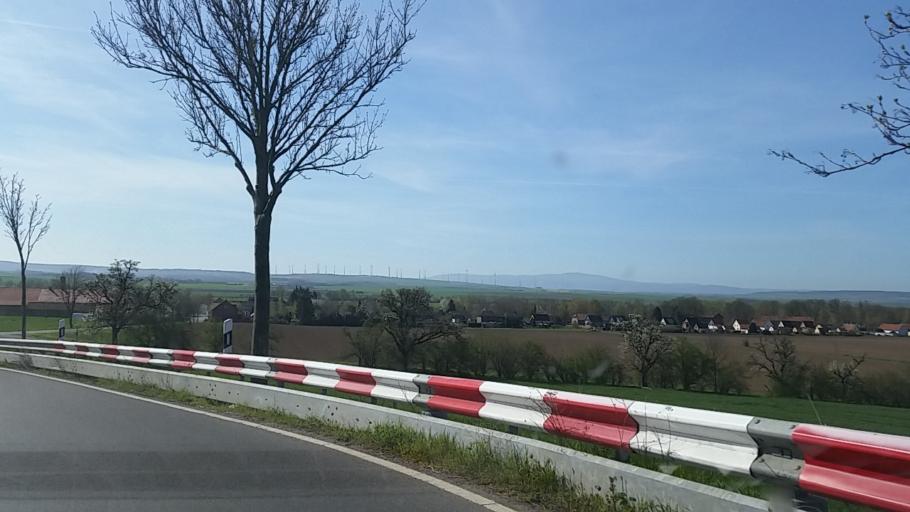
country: DE
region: Lower Saxony
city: Jerxheim
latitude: 52.0710
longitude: 10.8917
